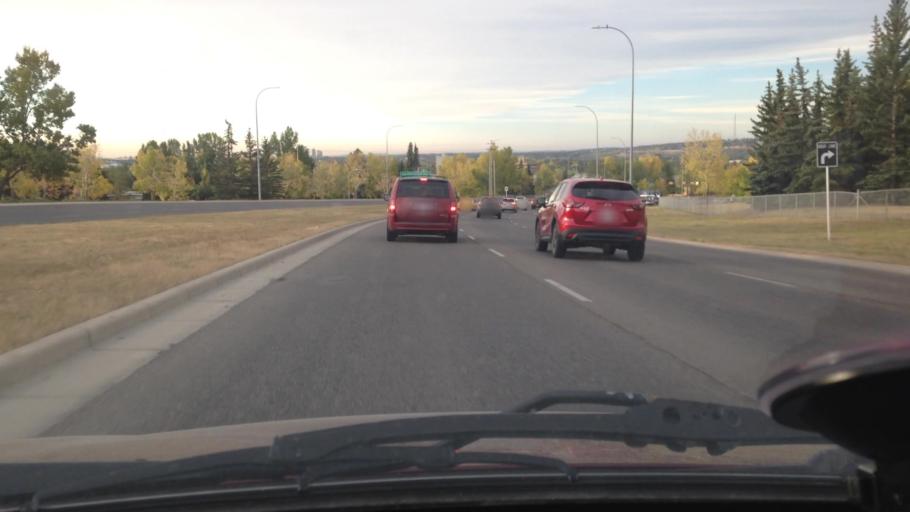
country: CA
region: Alberta
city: Calgary
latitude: 51.1057
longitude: -114.1408
